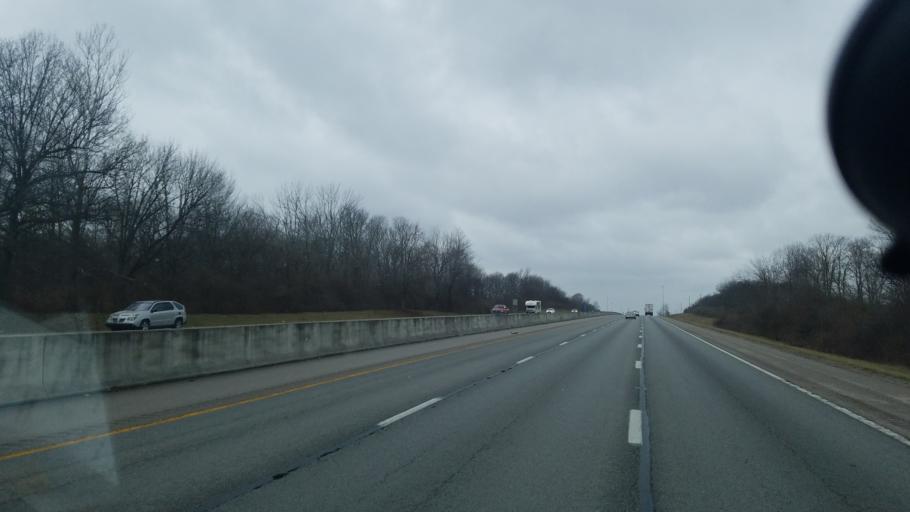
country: US
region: Kentucky
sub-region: Clark County
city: Winchester
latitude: 38.0413
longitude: -84.3077
